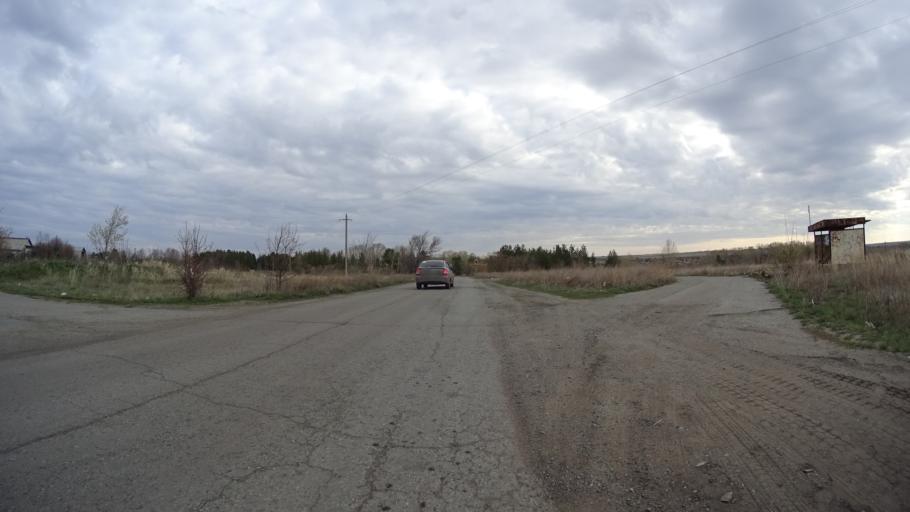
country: RU
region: Chelyabinsk
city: Troitsk
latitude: 54.0935
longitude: 61.4896
